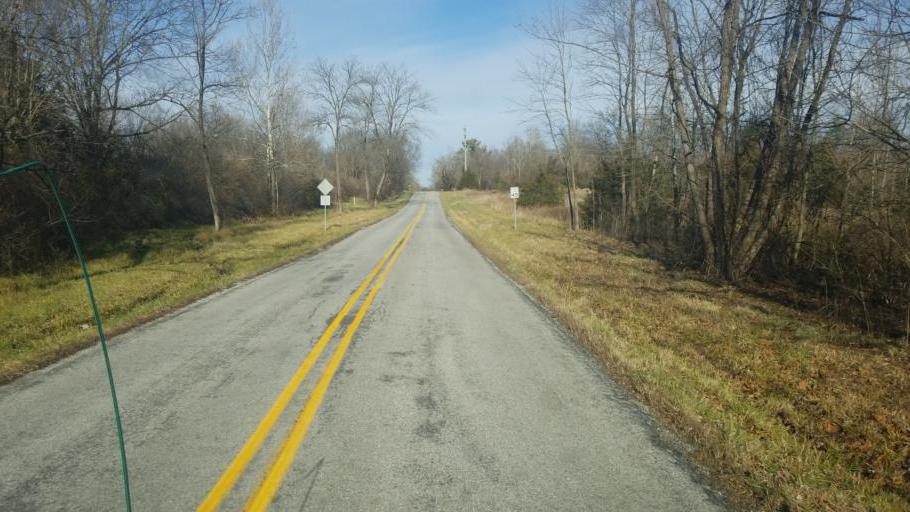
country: US
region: Illinois
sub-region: Jackson County
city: Carbondale
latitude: 37.6908
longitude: -89.2112
